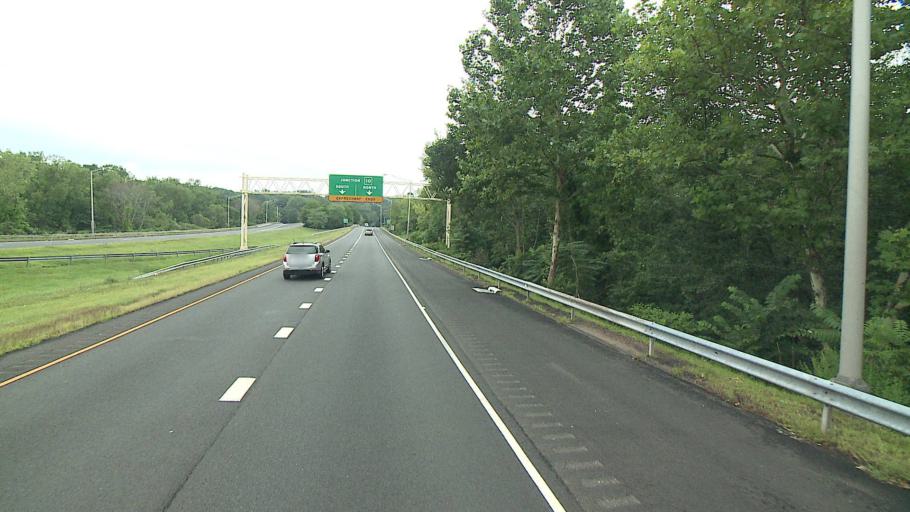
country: US
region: Connecticut
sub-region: New Haven County
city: Hamden
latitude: 41.3992
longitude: -72.8930
